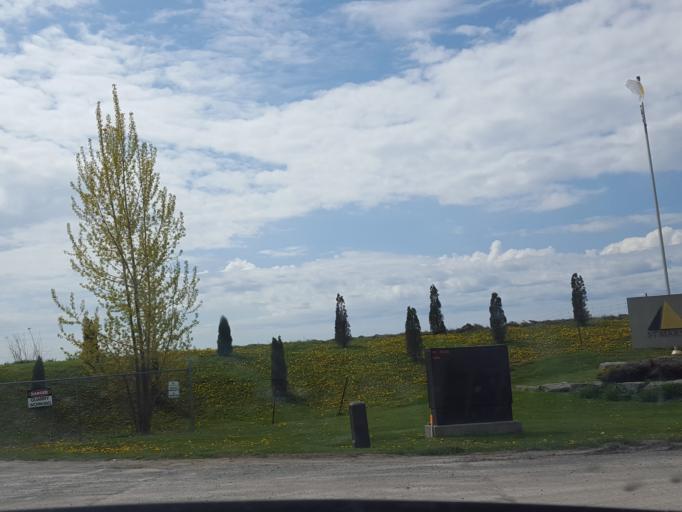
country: CA
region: Ontario
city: Oshawa
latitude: 43.8911
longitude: -78.6880
